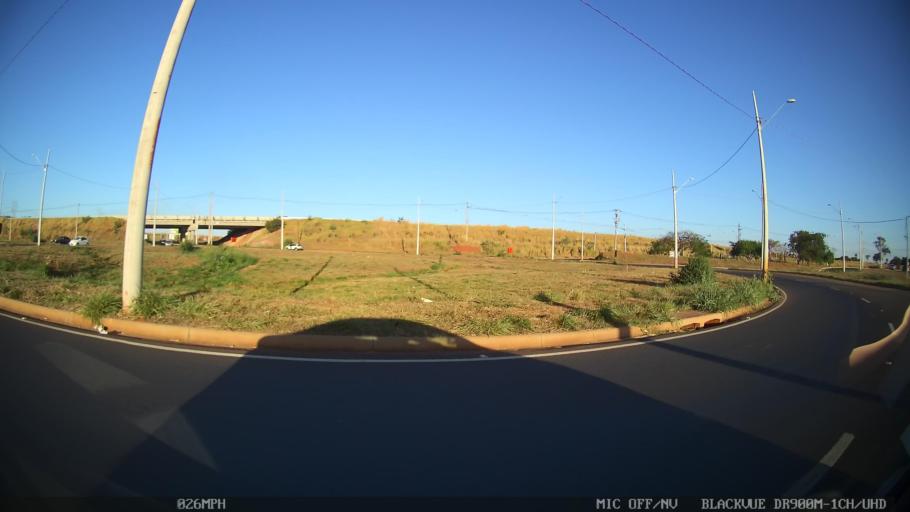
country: BR
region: Sao Paulo
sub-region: Sao Jose Do Rio Preto
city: Sao Jose do Rio Preto
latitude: -20.7619
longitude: -49.3474
